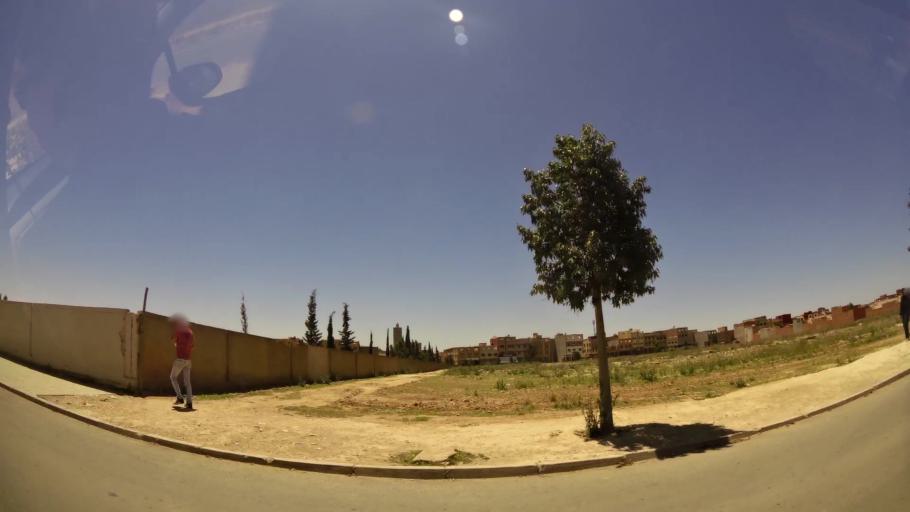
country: MA
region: Oriental
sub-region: Oujda-Angad
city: Oujda
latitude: 34.6778
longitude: -1.8689
